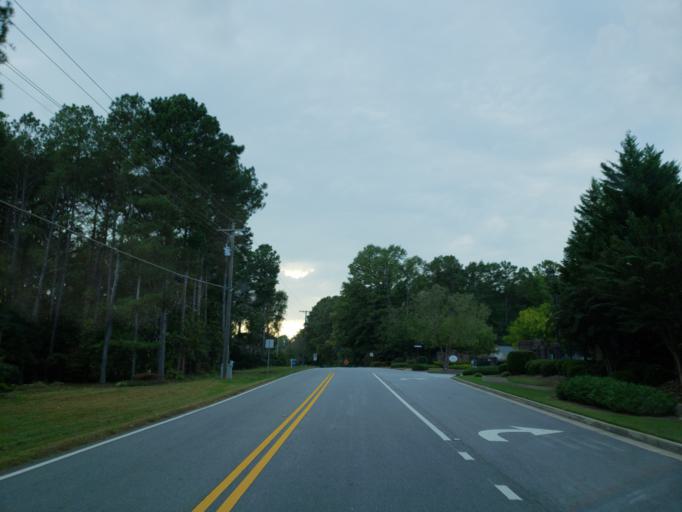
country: US
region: Georgia
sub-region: Cobb County
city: Powder Springs
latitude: 33.8429
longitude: -84.6909
